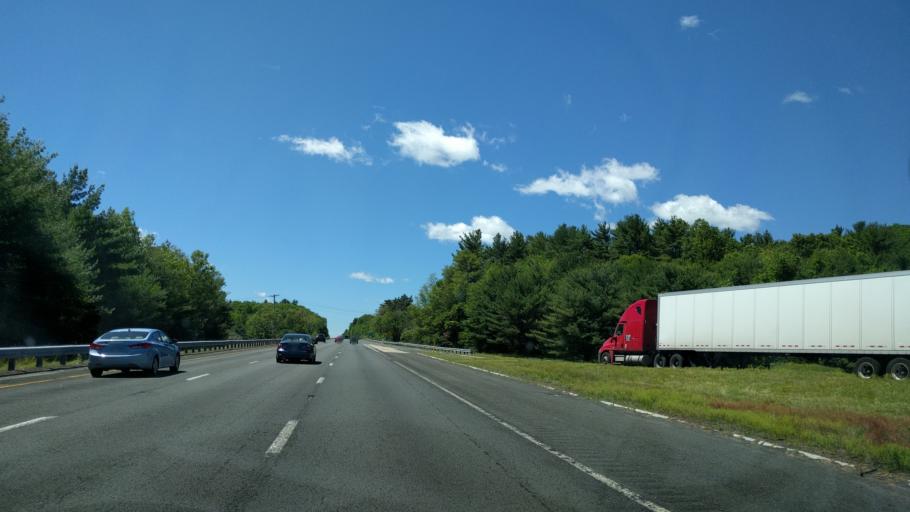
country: US
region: Massachusetts
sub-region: Worcester County
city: Fiskdale
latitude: 42.0685
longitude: -72.1080
